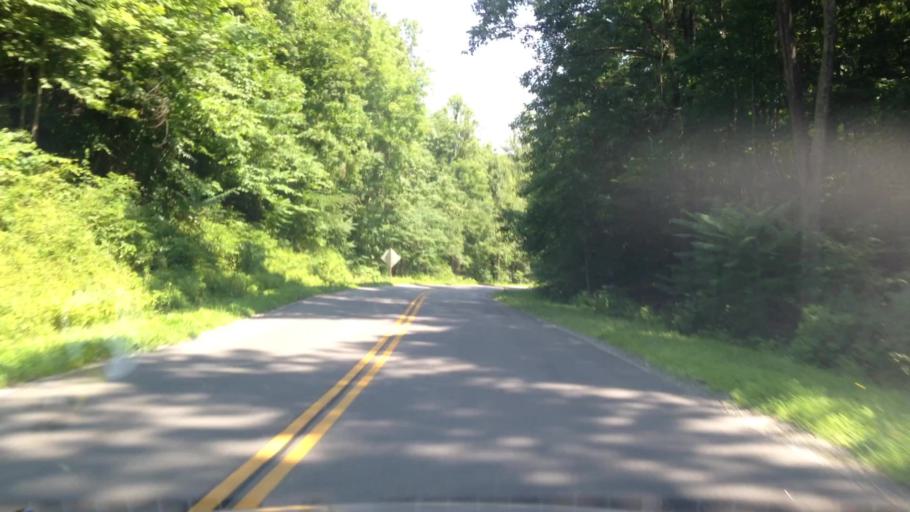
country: US
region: Virginia
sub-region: Patrick County
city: Patrick Springs
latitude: 36.5960
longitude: -80.1742
